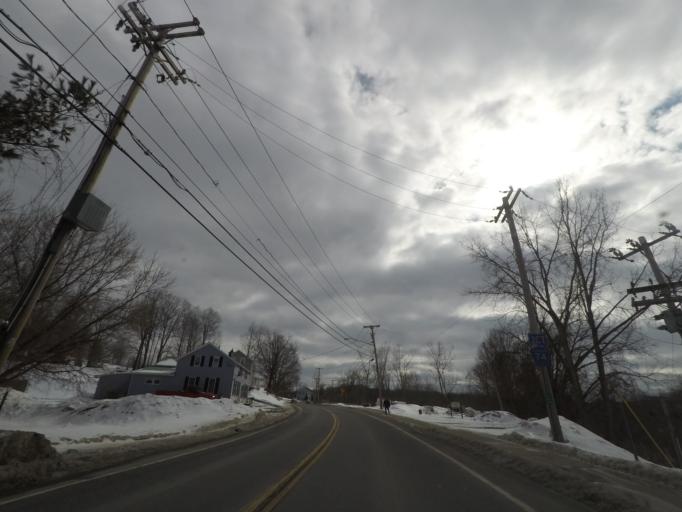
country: US
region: New York
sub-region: Washington County
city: Greenwich
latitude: 43.0864
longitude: -73.4943
